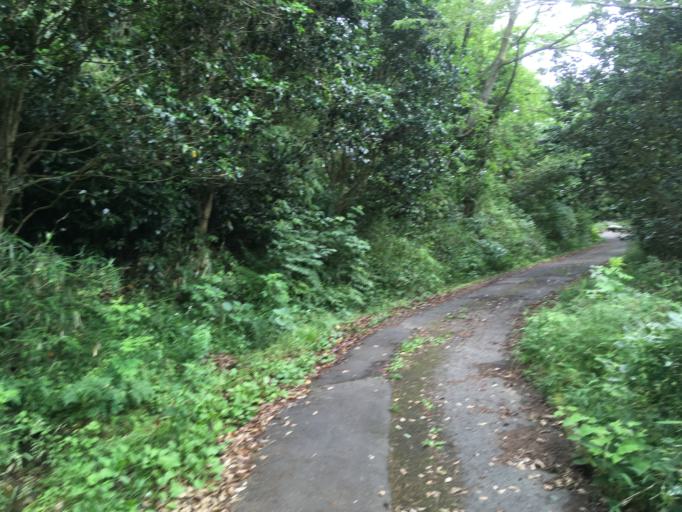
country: JP
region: Nara
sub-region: Ikoma-shi
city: Ikoma
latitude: 34.6839
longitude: 135.6756
